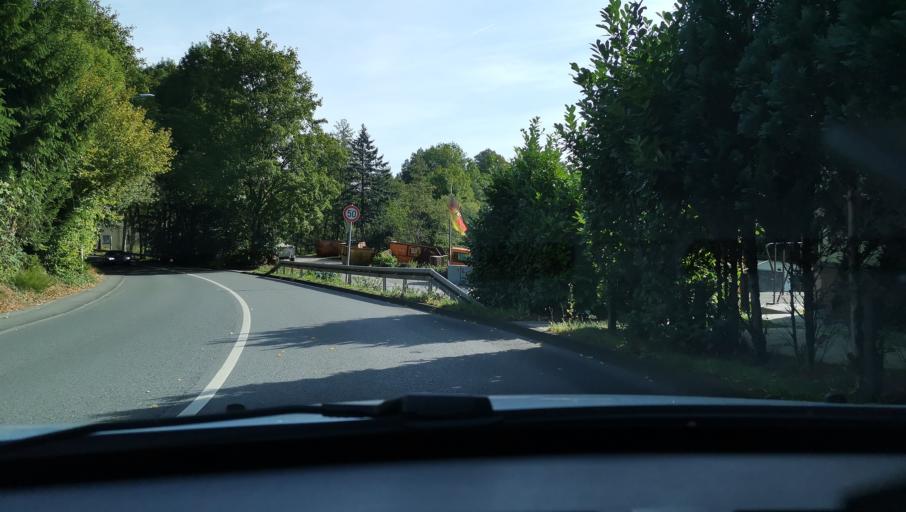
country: DE
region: North Rhine-Westphalia
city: Ennepetal
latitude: 51.3389
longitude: 7.3873
